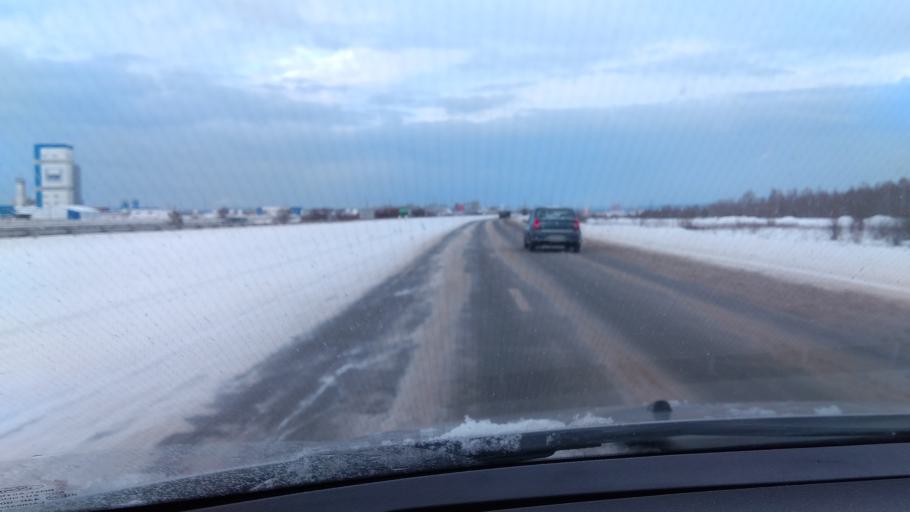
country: RU
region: Sverdlovsk
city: Tsementnyy
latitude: 57.4620
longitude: 60.1888
